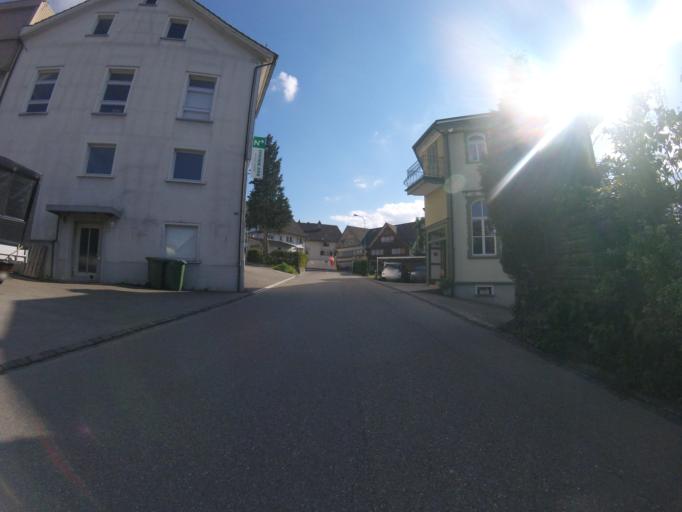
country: CH
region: Saint Gallen
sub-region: Wahlkreis Toggenburg
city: Mogelsberg
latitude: 47.3633
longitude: 9.1361
